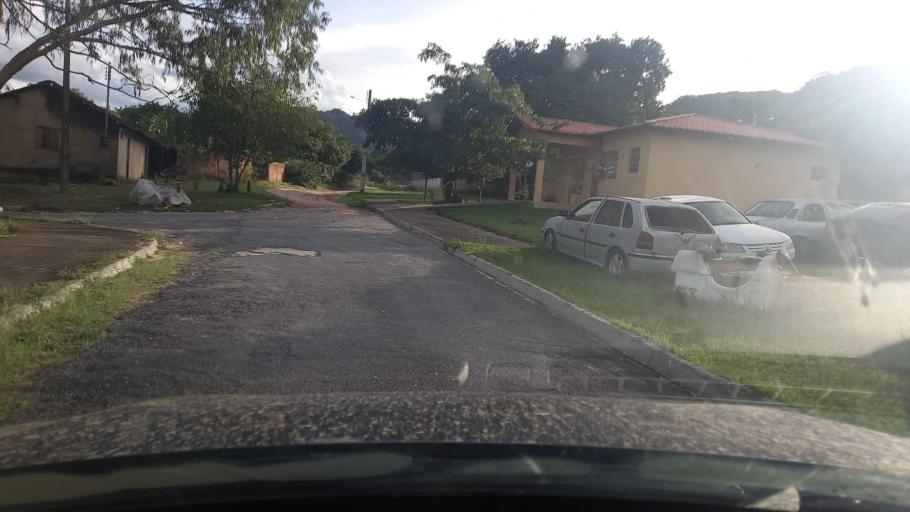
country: BR
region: Goias
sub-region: Cavalcante
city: Cavalcante
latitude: -13.7969
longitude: -47.4624
